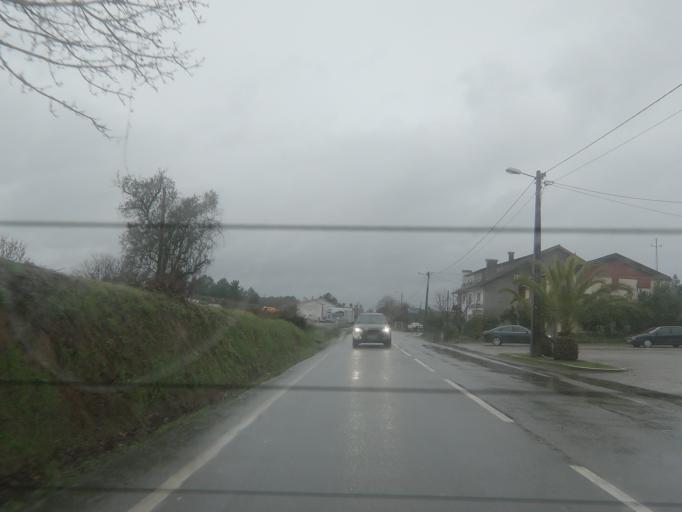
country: PT
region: Vila Real
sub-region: Vila Real
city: Vila Real
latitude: 41.2711
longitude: -7.7067
